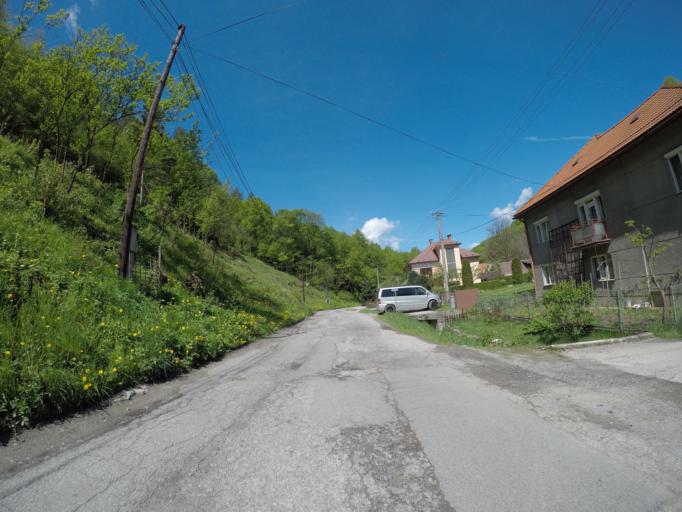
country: SK
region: Banskobystricky
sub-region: Okres Banska Bystrica
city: Banska Bystrica
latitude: 48.7211
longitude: 19.2219
